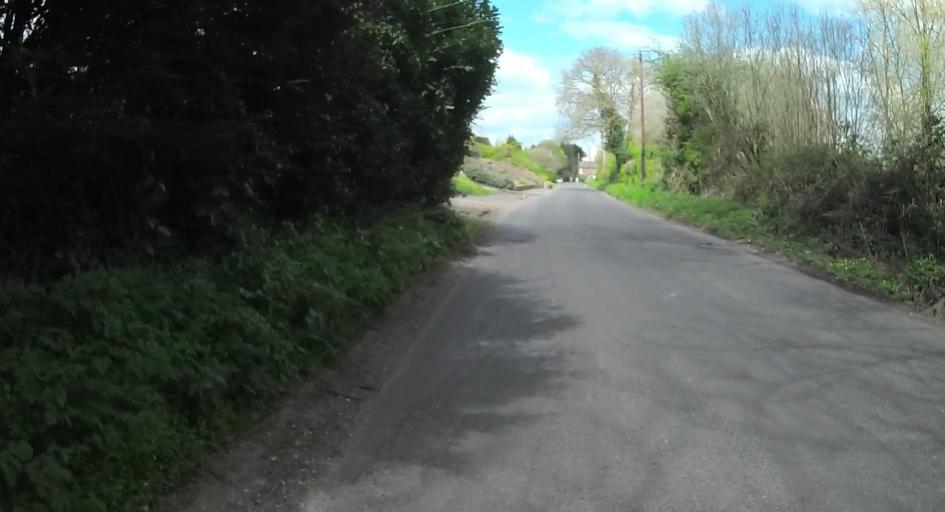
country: GB
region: England
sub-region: Hampshire
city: Abbotts Ann
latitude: 51.1122
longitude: -1.4995
